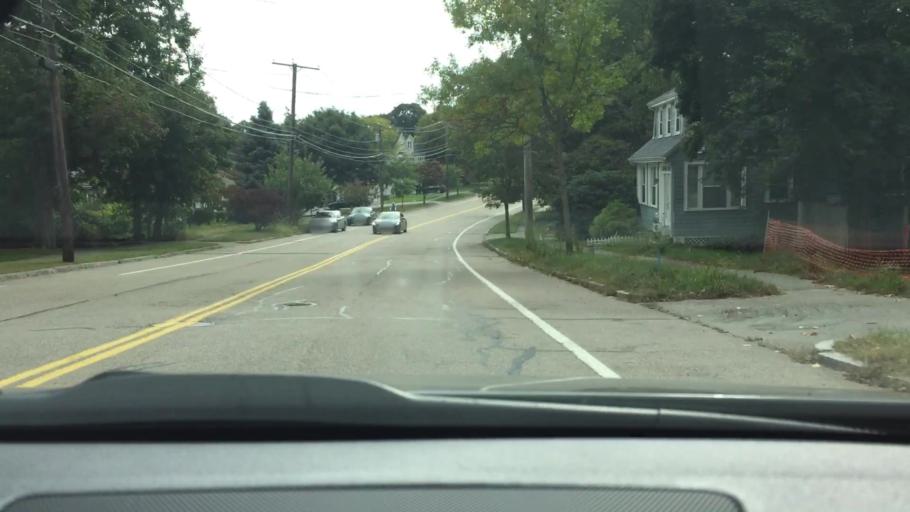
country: US
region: Massachusetts
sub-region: Norfolk County
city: Needham
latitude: 42.2758
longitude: -71.2043
